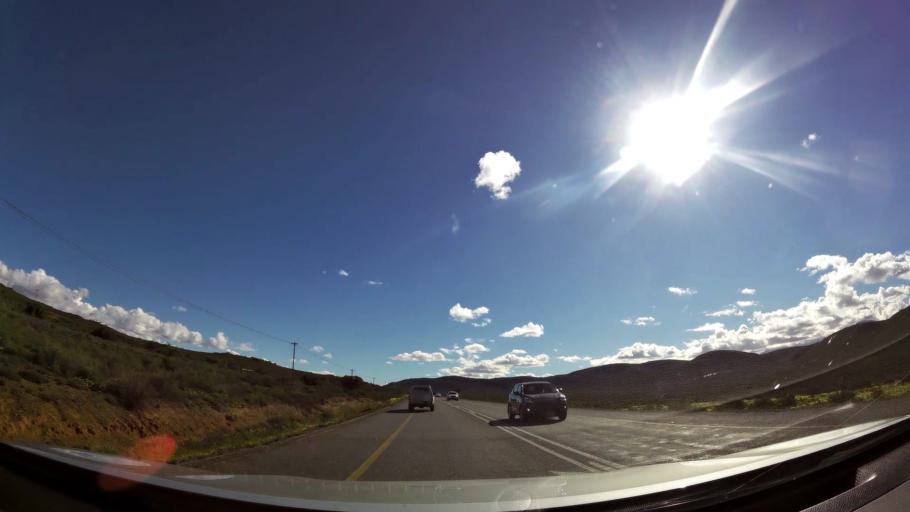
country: ZA
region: Western Cape
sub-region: Cape Winelands District Municipality
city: Worcester
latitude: -33.7389
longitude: 19.6890
